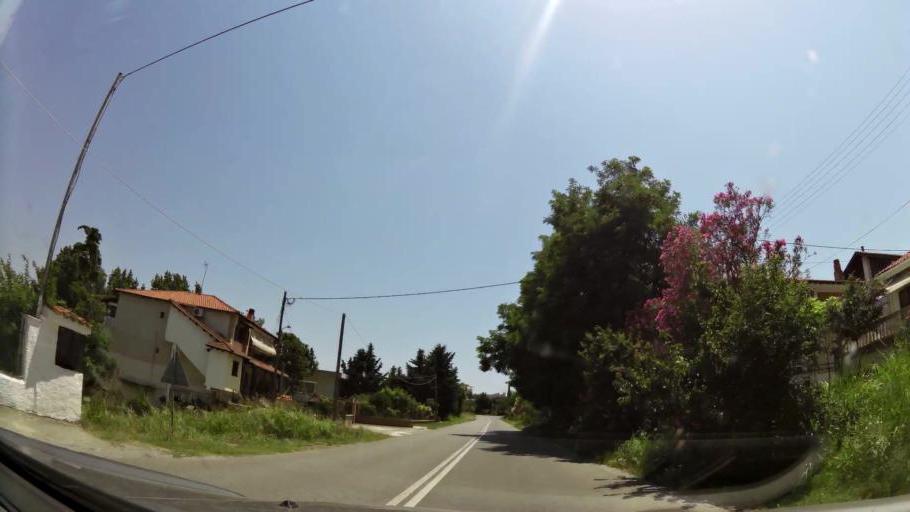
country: GR
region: Central Macedonia
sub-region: Nomos Thessalonikis
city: Trilofos
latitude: 40.4739
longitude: 22.9728
